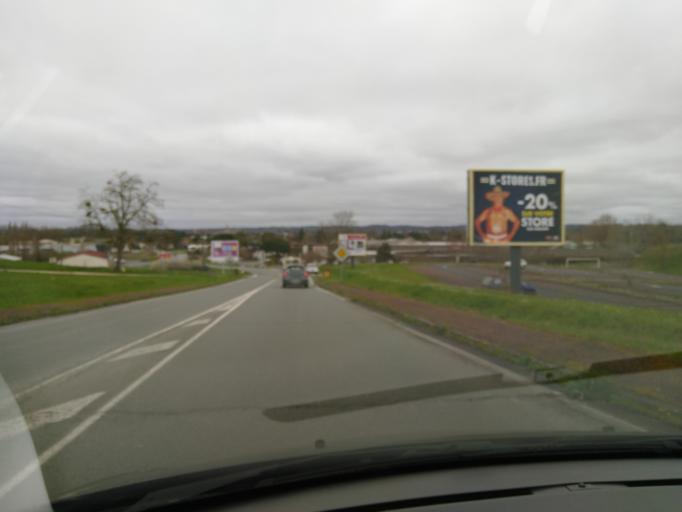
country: FR
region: Aquitaine
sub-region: Departement de la Dordogne
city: Bergerac
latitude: 44.8279
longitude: 0.5017
